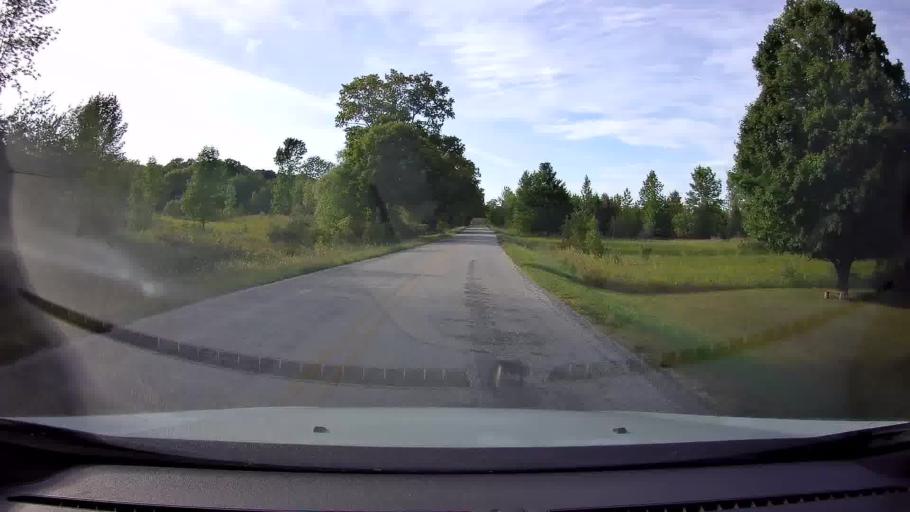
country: US
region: Wisconsin
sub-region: Door County
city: Sturgeon Bay
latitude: 45.1774
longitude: -87.1437
